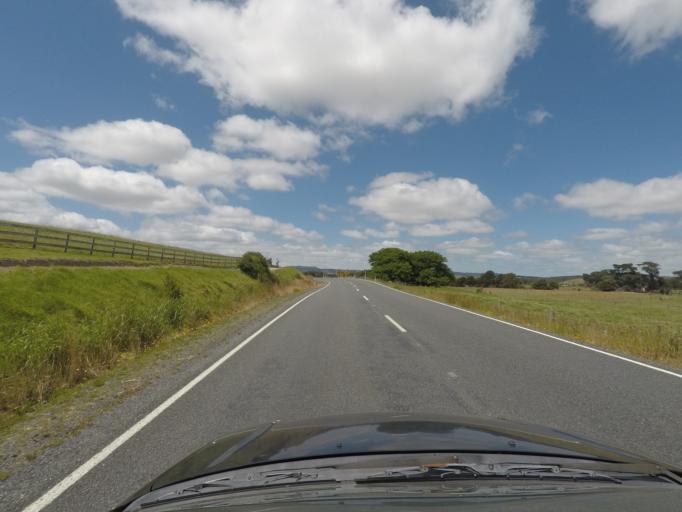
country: NZ
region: Northland
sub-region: Whangarei
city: Ruakaka
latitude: -35.9890
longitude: 174.4566
